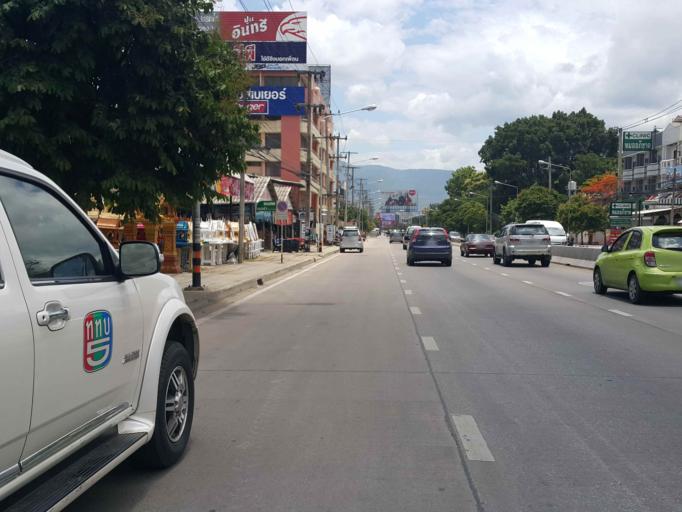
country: TH
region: Chiang Mai
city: Chiang Mai
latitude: 18.7624
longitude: 98.9945
